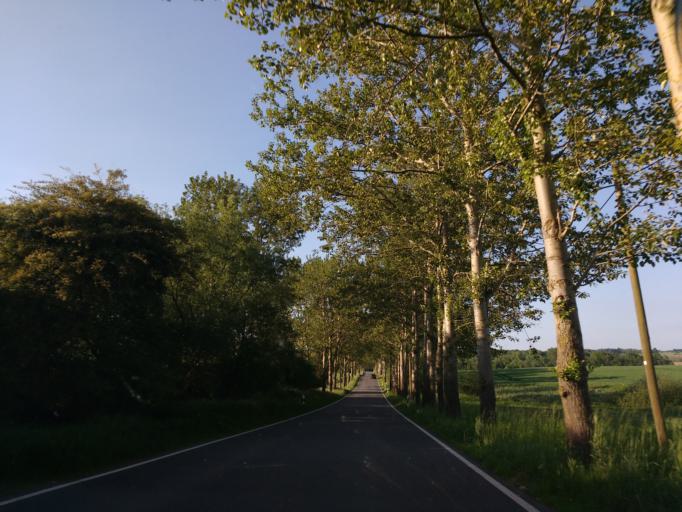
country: DE
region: Mecklenburg-Vorpommern
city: Lubow
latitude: 53.8604
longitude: 11.5270
